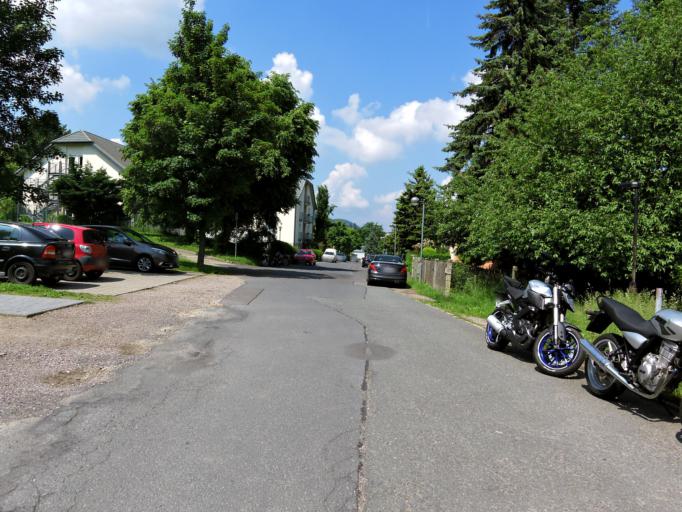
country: DE
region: Thuringia
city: Friedrichroda
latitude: 50.8552
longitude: 10.5749
